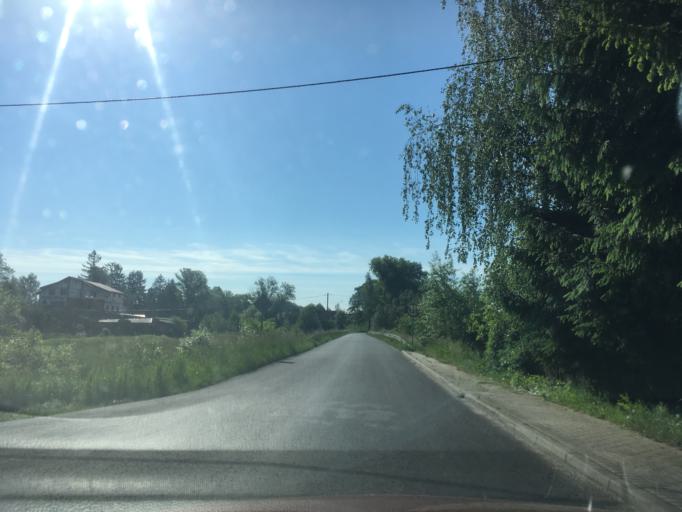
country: PL
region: Lower Silesian Voivodeship
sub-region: Powiat zgorzelecki
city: Zgorzelec
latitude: 51.1120
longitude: 15.0304
